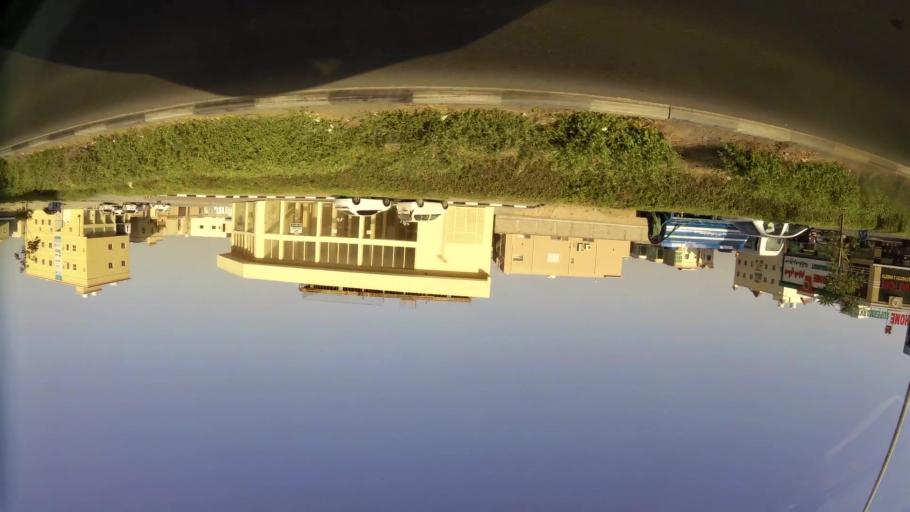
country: AE
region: Ajman
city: Ajman
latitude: 25.3813
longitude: 55.5071
